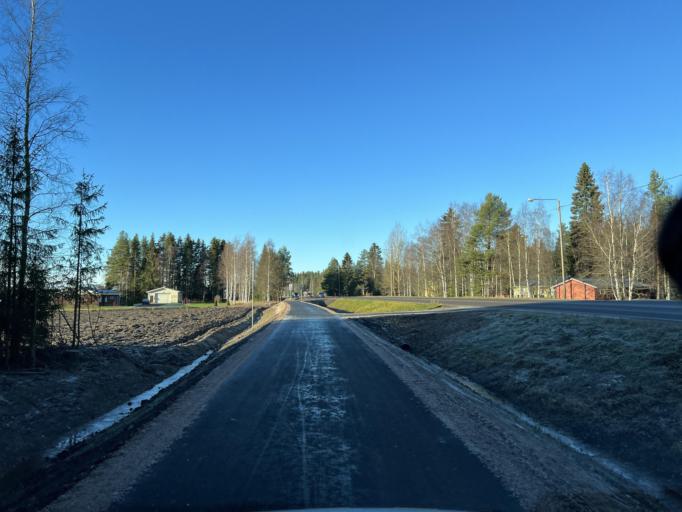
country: FI
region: Northern Ostrobothnia
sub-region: Nivala-Haapajaervi
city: Nivala
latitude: 63.9504
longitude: 24.9163
